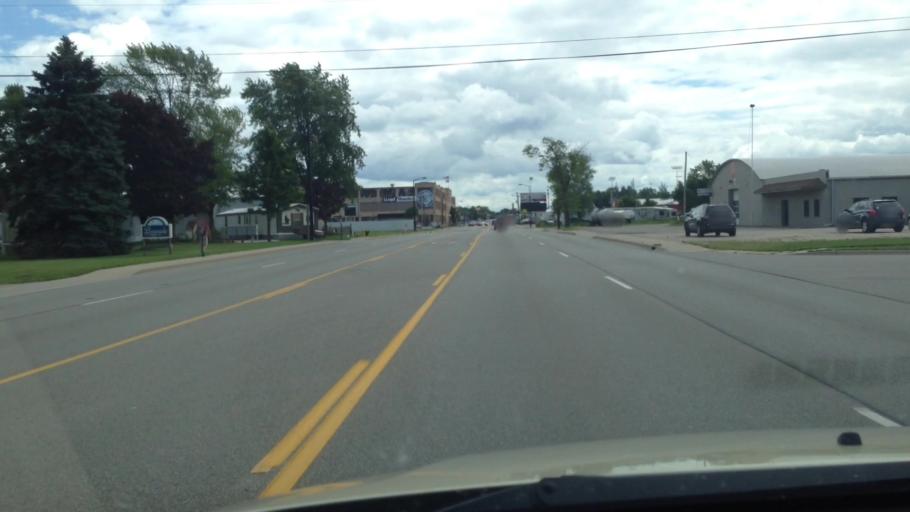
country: US
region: Michigan
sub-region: Menominee County
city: Menominee
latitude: 45.1298
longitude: -87.6128
